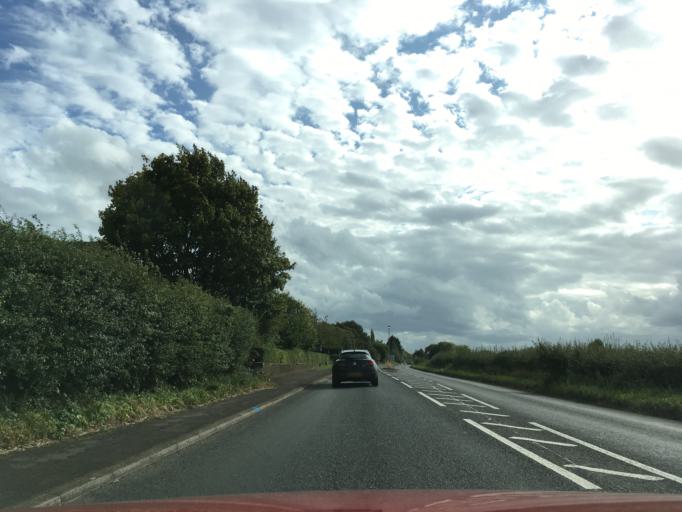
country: GB
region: England
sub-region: South Gloucestershire
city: Falfield
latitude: 51.6435
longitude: -2.4556
